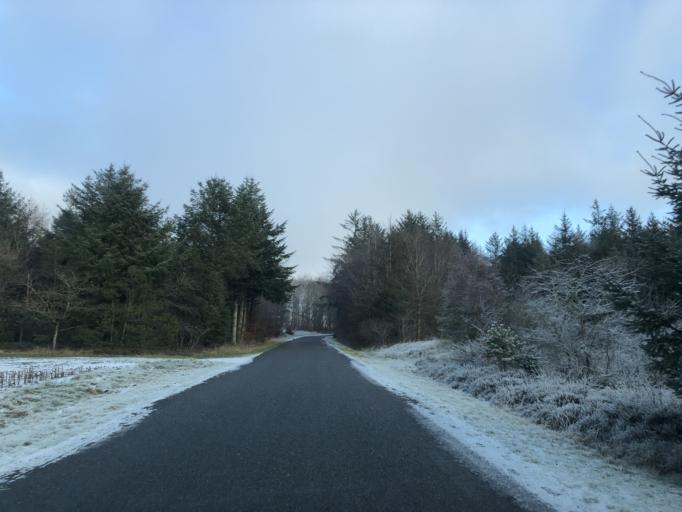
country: DK
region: Central Jutland
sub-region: Holstebro Kommune
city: Ulfborg
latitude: 56.2057
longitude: 8.3447
